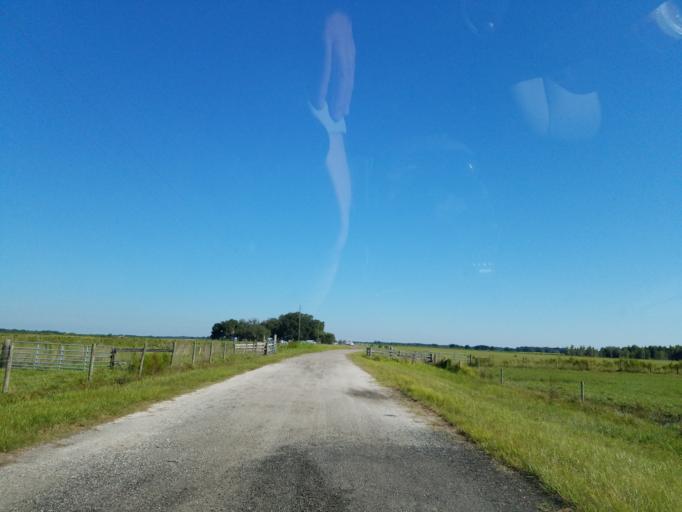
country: US
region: Florida
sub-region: Pasco County
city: Wesley Chapel
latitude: 28.3310
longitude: -82.3977
